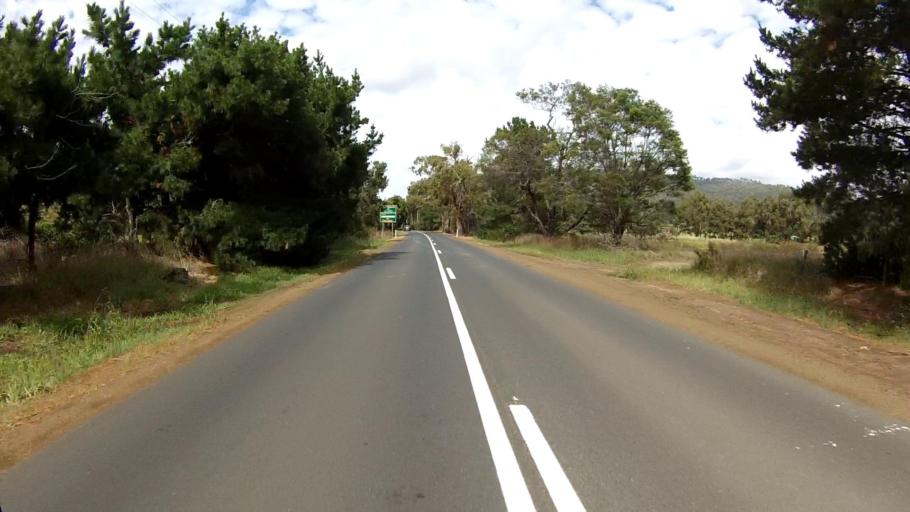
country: AU
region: Tasmania
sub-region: Clarence
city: Cambridge
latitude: -42.7616
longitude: 147.3976
